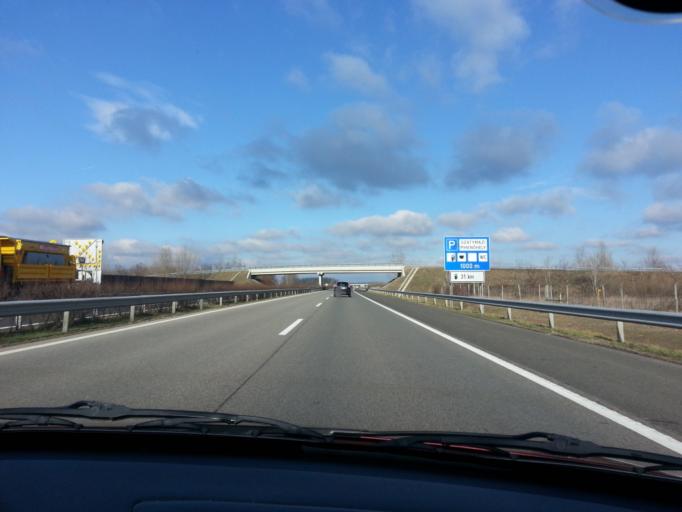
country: HU
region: Csongrad
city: Szatymaz
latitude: 46.3576
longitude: 20.0042
